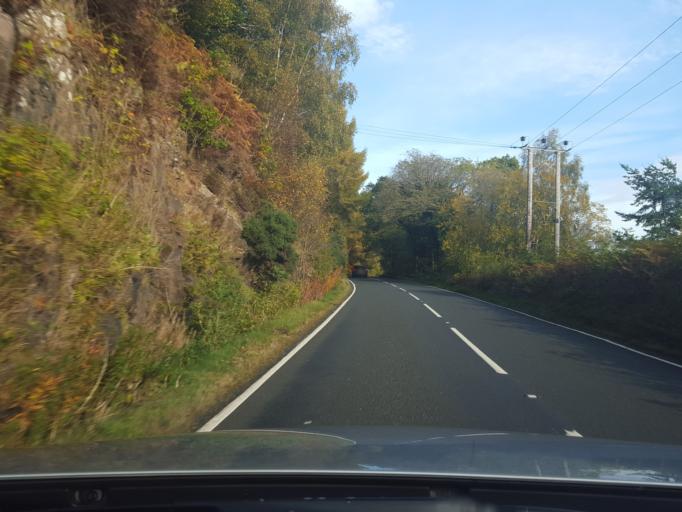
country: GB
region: Scotland
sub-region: Highland
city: Beauly
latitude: 57.2601
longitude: -4.5225
